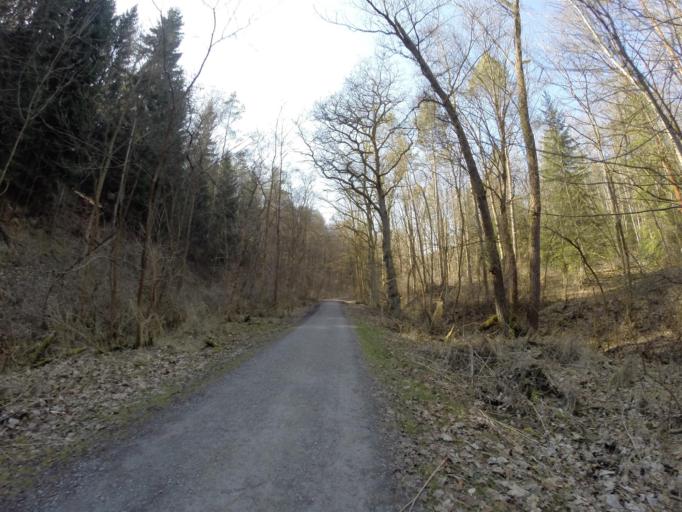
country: DE
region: Thuringia
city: Grossschwabhausen
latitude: 50.9460
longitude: 11.5278
